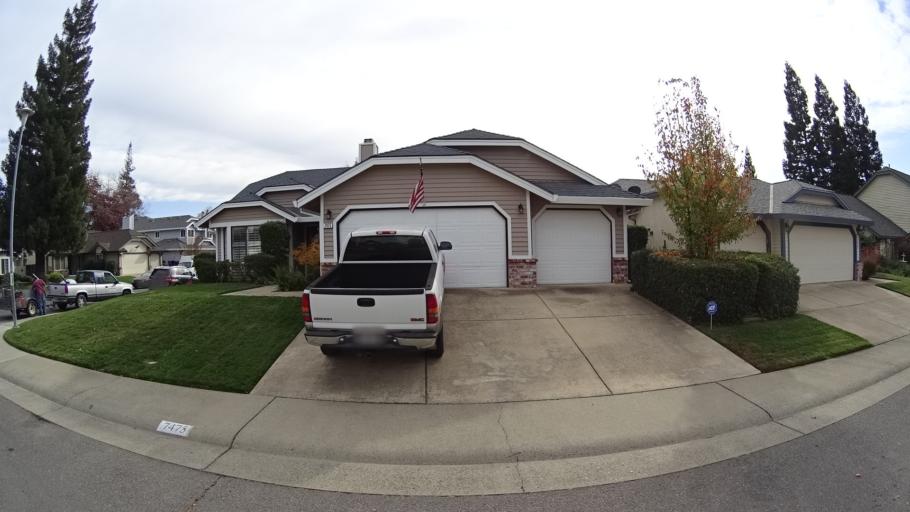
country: US
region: California
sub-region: Sacramento County
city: Citrus Heights
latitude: 38.7028
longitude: -121.2678
